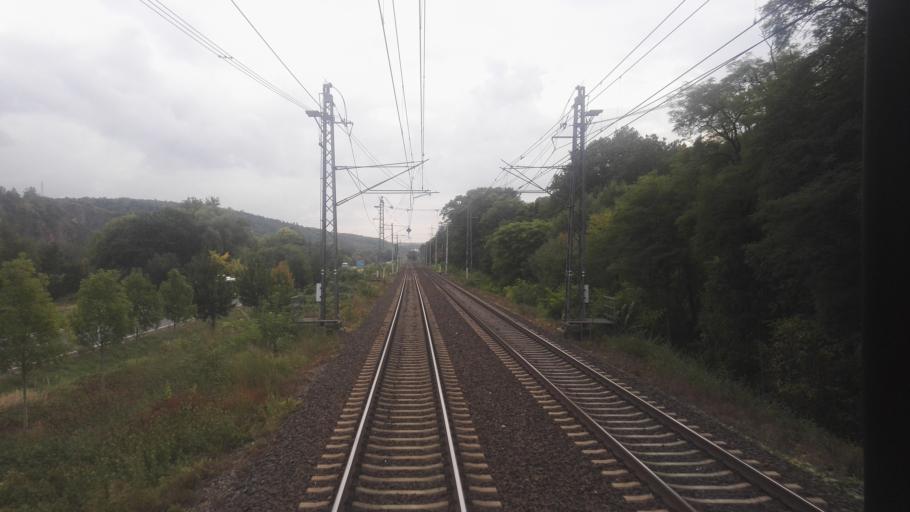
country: CZ
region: Central Bohemia
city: Roztoky
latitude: 50.1505
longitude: 14.3974
